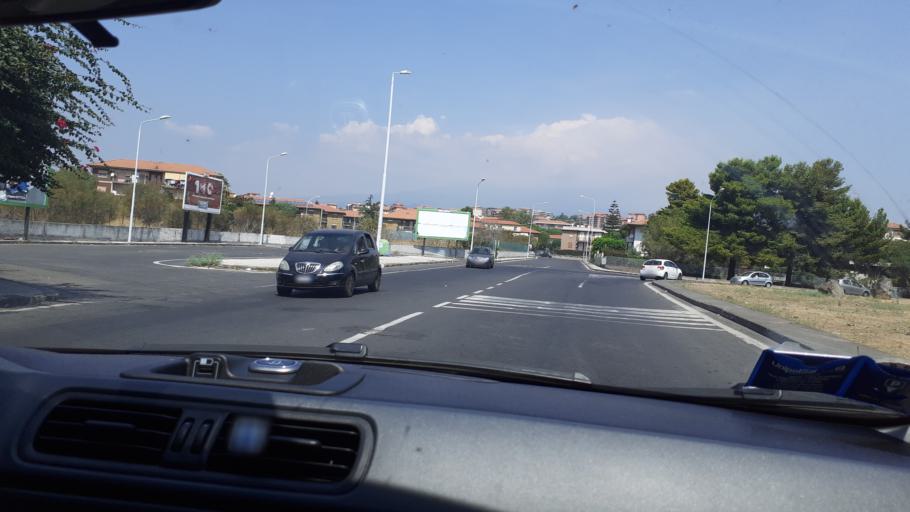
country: IT
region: Sicily
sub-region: Catania
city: Misterbianco
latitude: 37.5149
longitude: 15.0561
